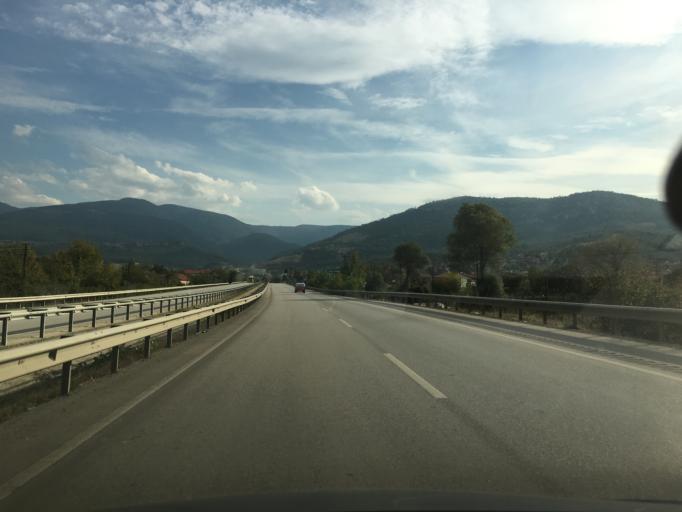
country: TR
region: Karabuk
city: Karabuk
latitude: 41.1083
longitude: 32.6686
